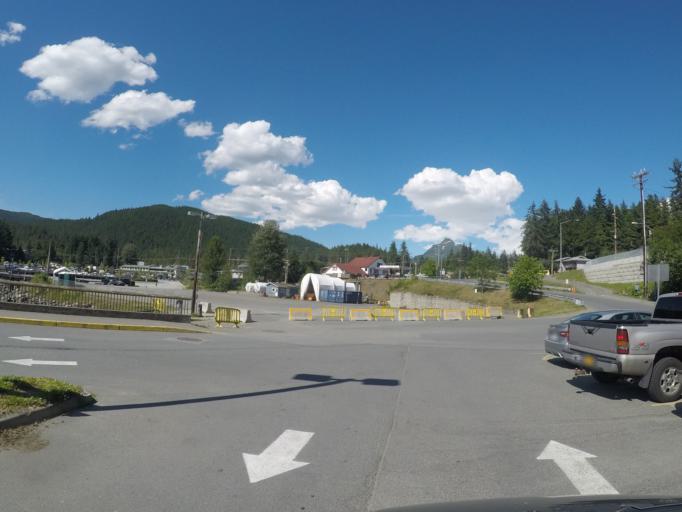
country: US
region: Alaska
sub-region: Juneau City and Borough
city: Juneau
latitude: 58.3849
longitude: -134.6452
